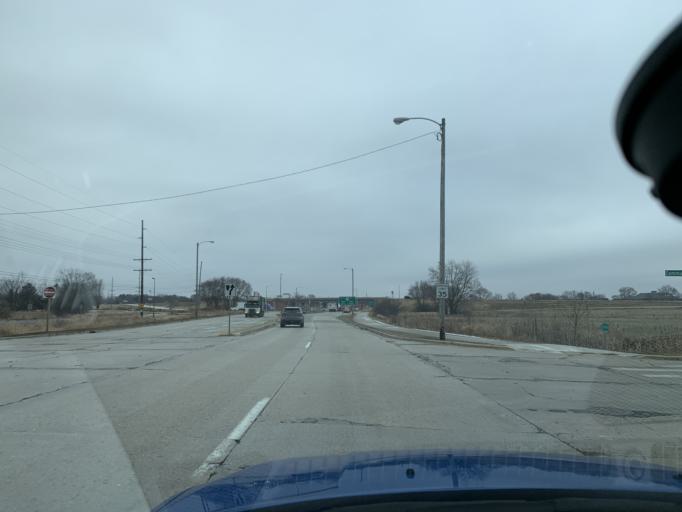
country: US
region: Wisconsin
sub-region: Dane County
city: Sun Prairie
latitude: 43.1874
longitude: -89.2371
